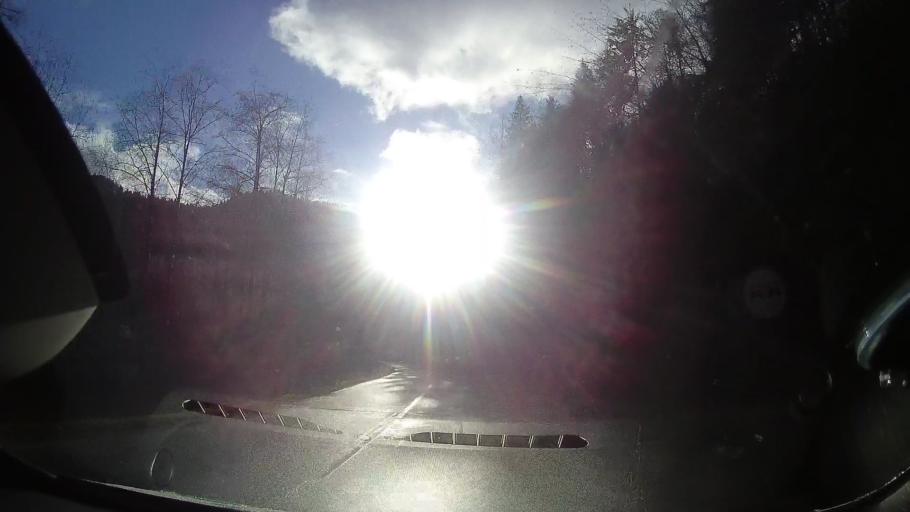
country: RO
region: Alba
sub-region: Comuna Vadu Motilor
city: Vadu Motilor
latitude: 46.4165
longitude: 22.9688
